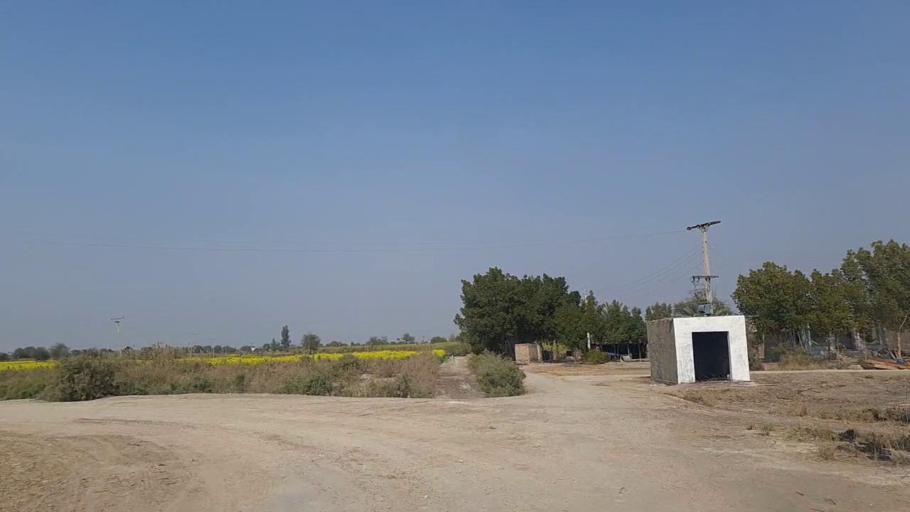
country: PK
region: Sindh
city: Daur
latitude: 26.4881
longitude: 68.4514
